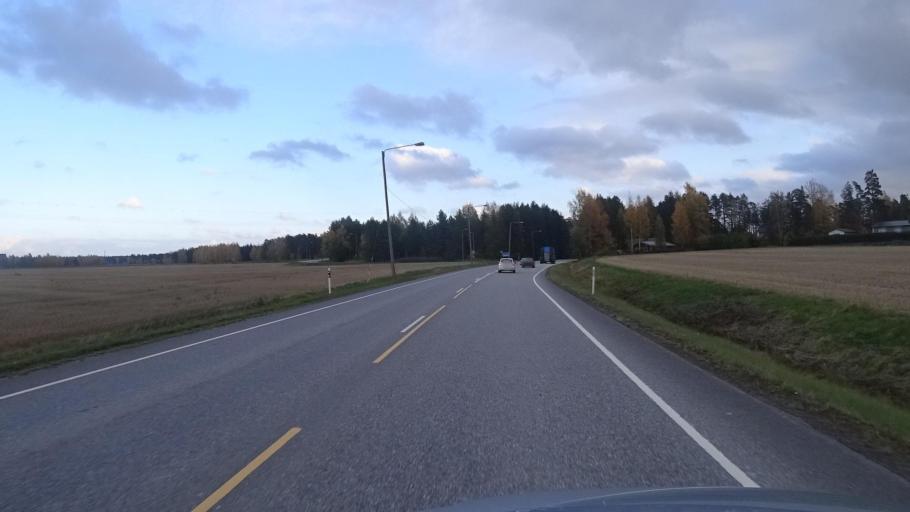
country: FI
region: Satakunta
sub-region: Rauma
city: Saekylae
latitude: 61.0398
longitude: 22.3829
